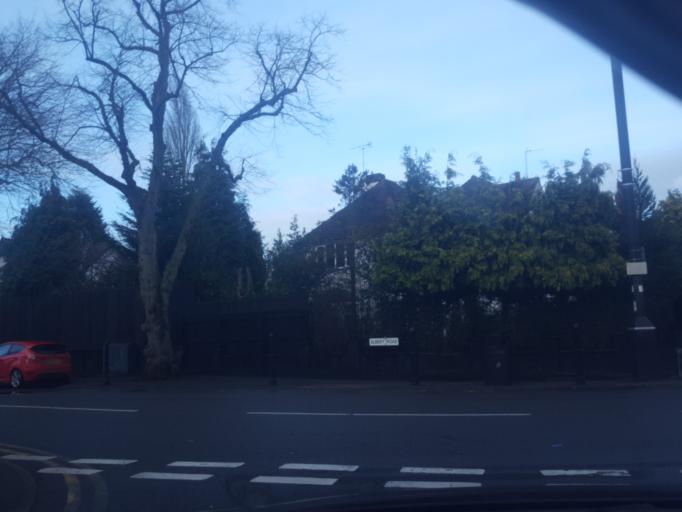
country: GB
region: England
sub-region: Wolverhampton
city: Wolverhampton
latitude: 52.5910
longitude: -2.1431
